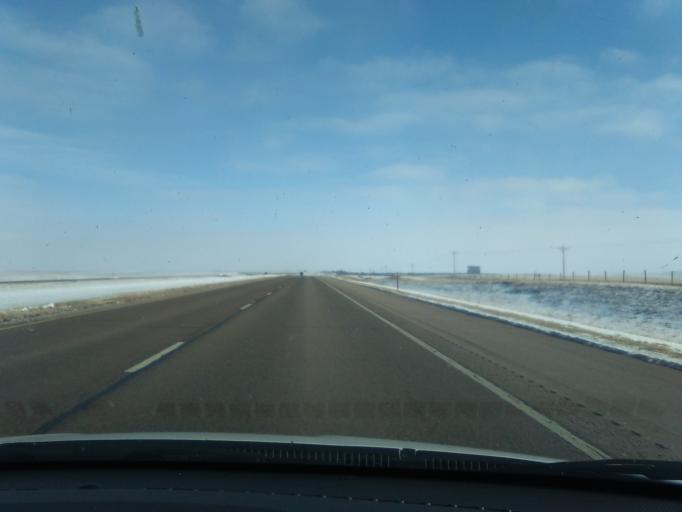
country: US
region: Nebraska
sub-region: Kimball County
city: Kimball
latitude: 41.1917
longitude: -103.7921
